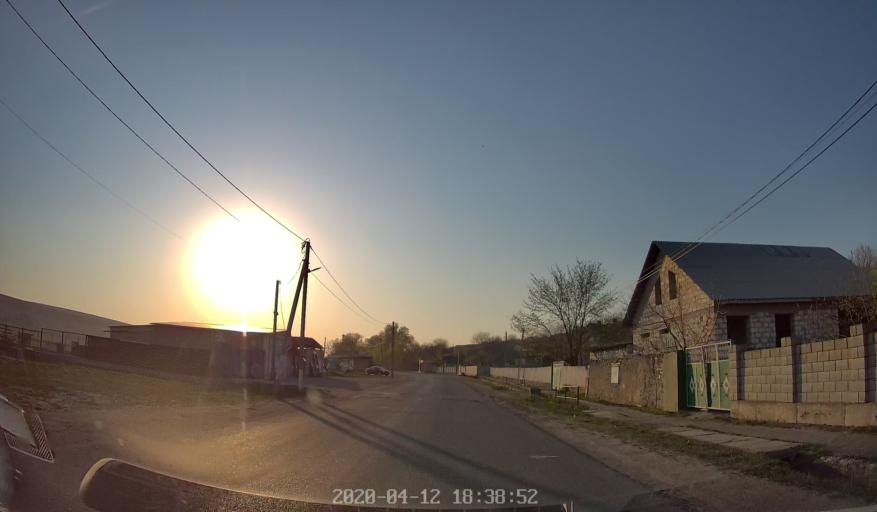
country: MD
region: Chisinau
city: Vadul lui Voda
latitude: 47.1261
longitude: 28.9949
